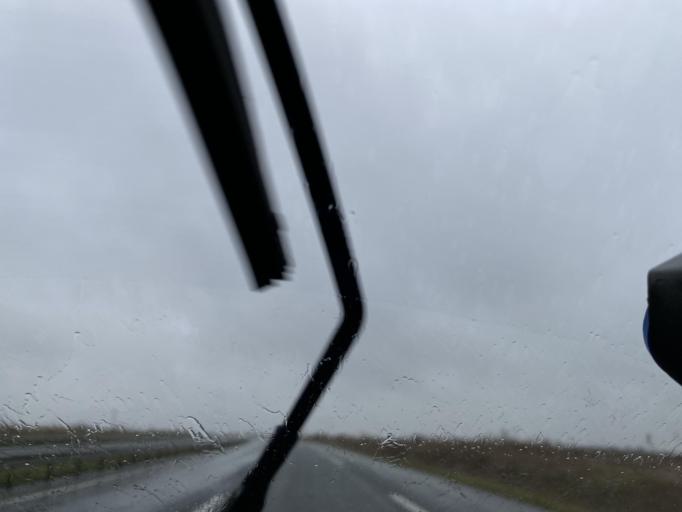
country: FR
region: Centre
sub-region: Departement d'Eure-et-Loir
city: Bailleau-l'Eveque
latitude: 48.5410
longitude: 1.4498
